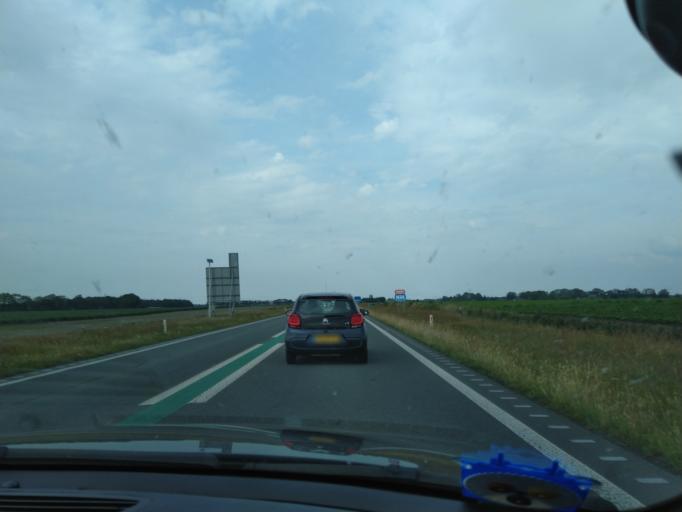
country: NL
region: Drenthe
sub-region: Gemeente Coevorden
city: Dalen
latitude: 52.7132
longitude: 6.7607
